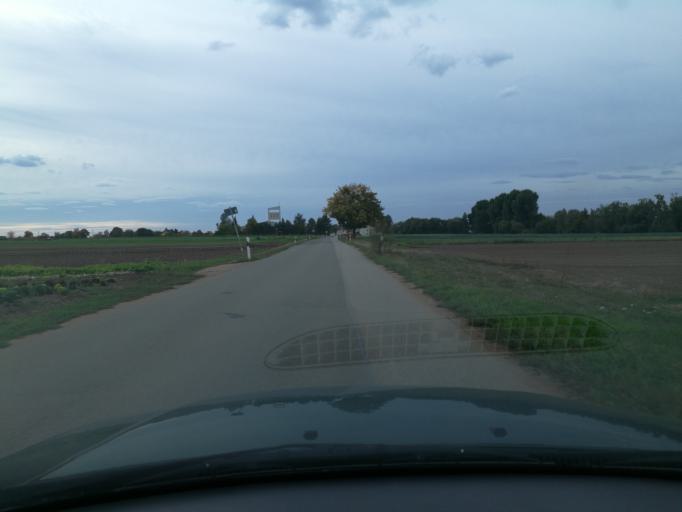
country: DE
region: Bavaria
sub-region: Regierungsbezirk Mittelfranken
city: Wetzendorf
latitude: 49.5116
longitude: 11.0413
